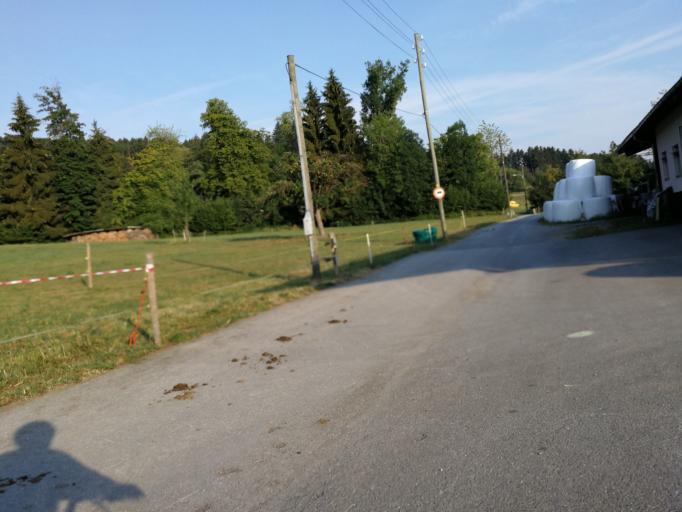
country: CH
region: Zurich
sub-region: Bezirk Meilen
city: Oetwil am See
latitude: 47.2759
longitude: 8.7159
